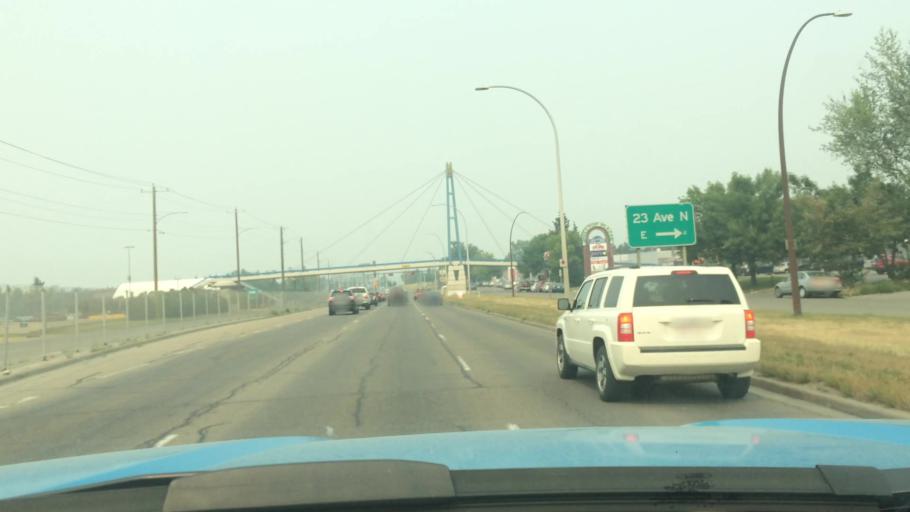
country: CA
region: Alberta
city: Calgary
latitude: 51.0694
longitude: -114.1178
